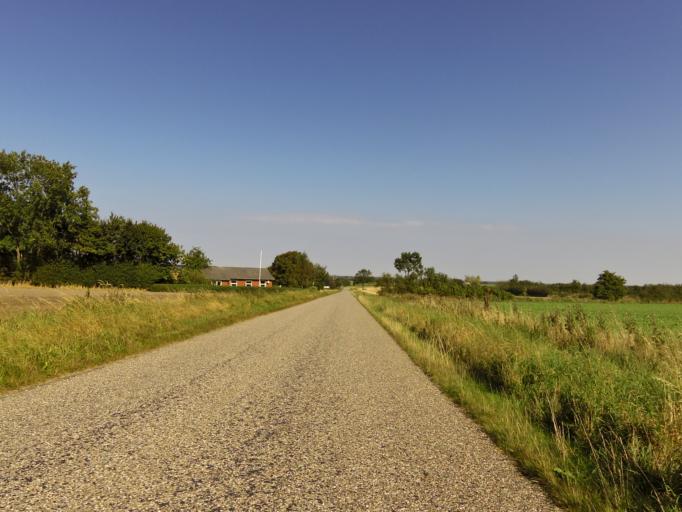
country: DK
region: South Denmark
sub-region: Vejen Kommune
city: Rodding
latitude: 55.3289
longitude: 9.1185
